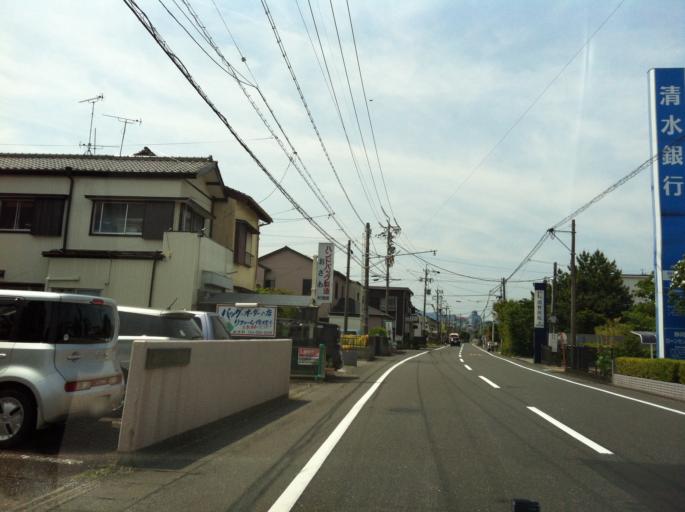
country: JP
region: Shizuoka
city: Shizuoka-shi
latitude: 34.9928
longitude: 138.4035
